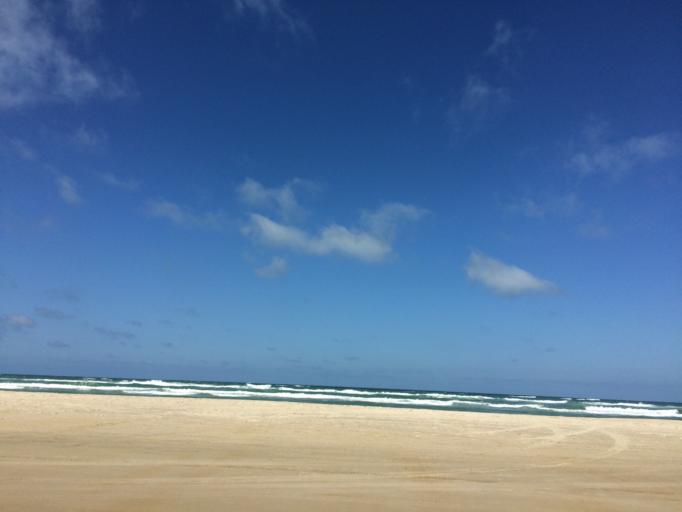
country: DK
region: North Denmark
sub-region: Jammerbugt Kommune
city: Brovst
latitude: 57.2239
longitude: 9.5372
